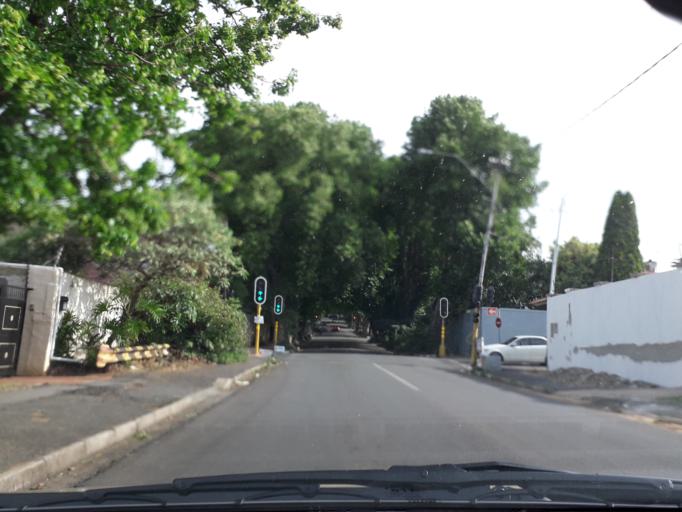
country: ZA
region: Gauteng
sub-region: City of Johannesburg Metropolitan Municipality
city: Johannesburg
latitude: -26.1621
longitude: 28.0886
